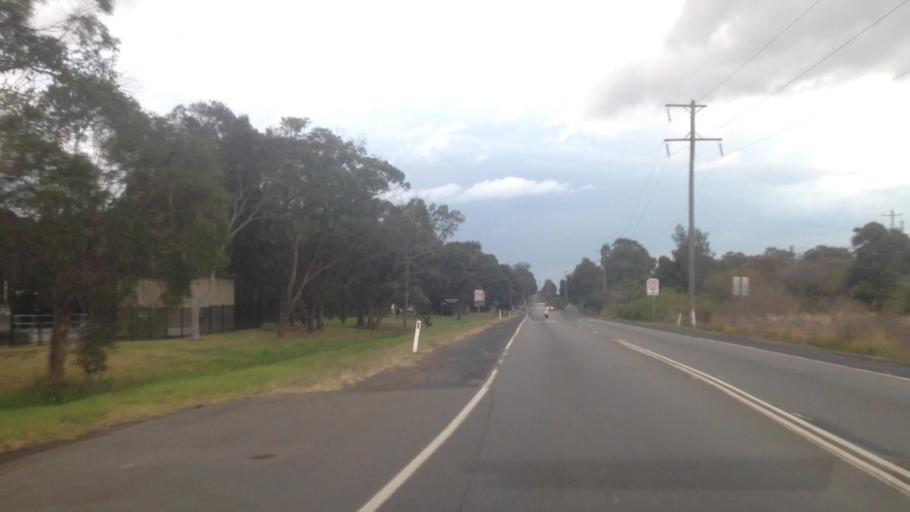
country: AU
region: New South Wales
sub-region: Wyong Shire
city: Chittaway Bay
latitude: -33.2788
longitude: 151.4275
